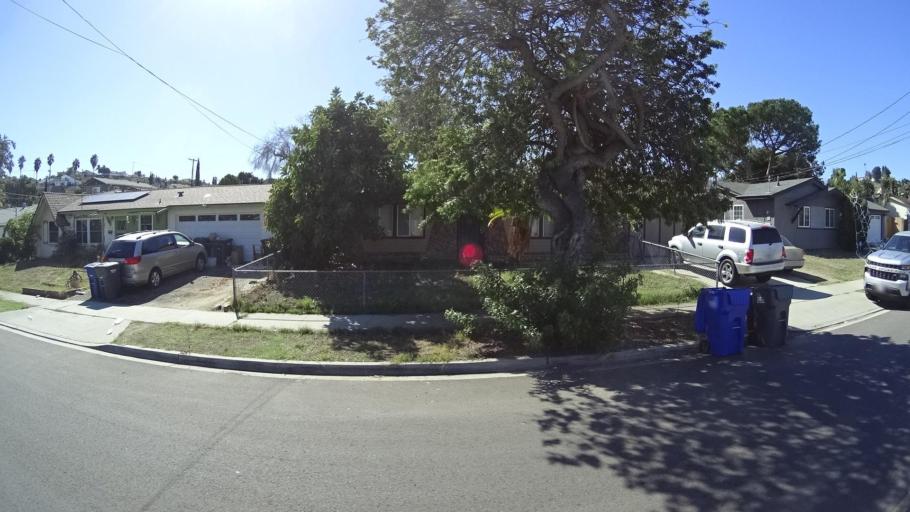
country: US
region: California
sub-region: San Diego County
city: La Presa
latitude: 32.7027
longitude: -117.0183
